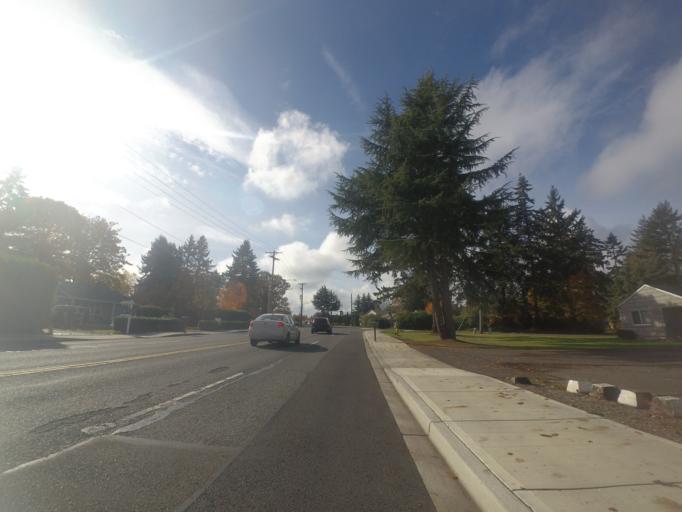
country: US
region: Washington
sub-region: Pierce County
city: Lakewood
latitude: 47.1743
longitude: -122.5149
